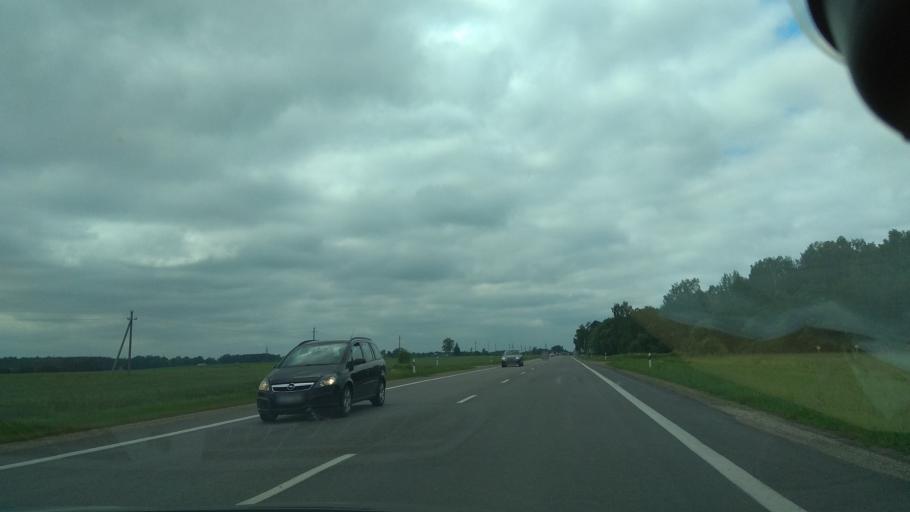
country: LT
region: Panevezys
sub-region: Panevezys City
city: Panevezys
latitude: 55.7343
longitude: 24.2507
